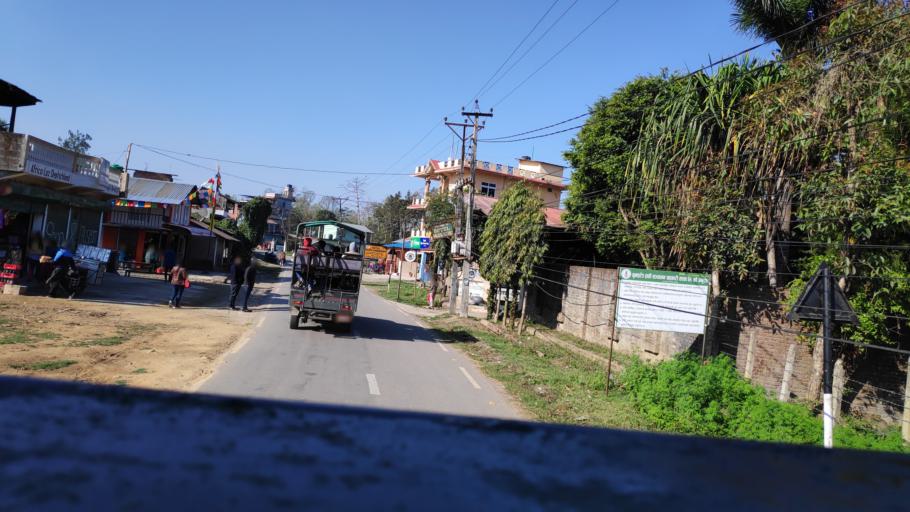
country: NP
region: Central Region
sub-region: Narayani Zone
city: Bharatpur
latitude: 27.5758
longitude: 84.5034
